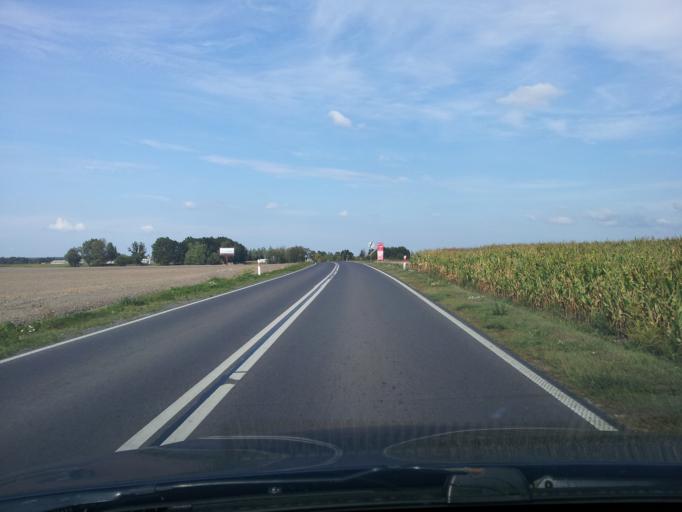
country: PL
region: Kujawsko-Pomorskie
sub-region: Powiat brodnicki
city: Brodnica
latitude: 53.2084
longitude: 19.3847
